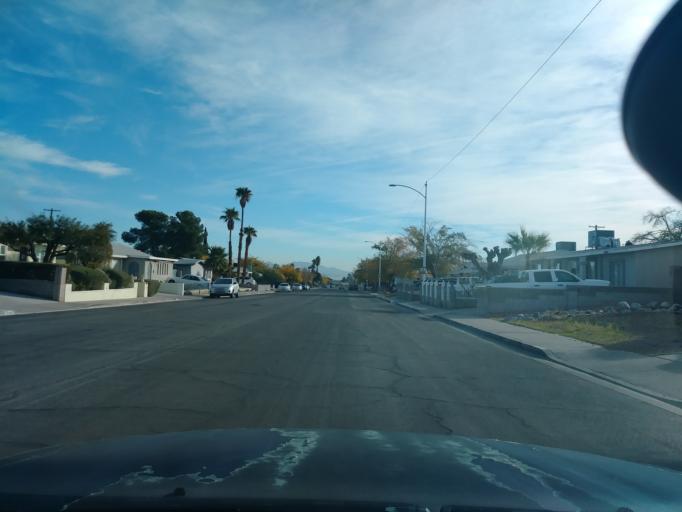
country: US
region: Nevada
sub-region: Clark County
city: Spring Valley
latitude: 36.1622
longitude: -115.2359
